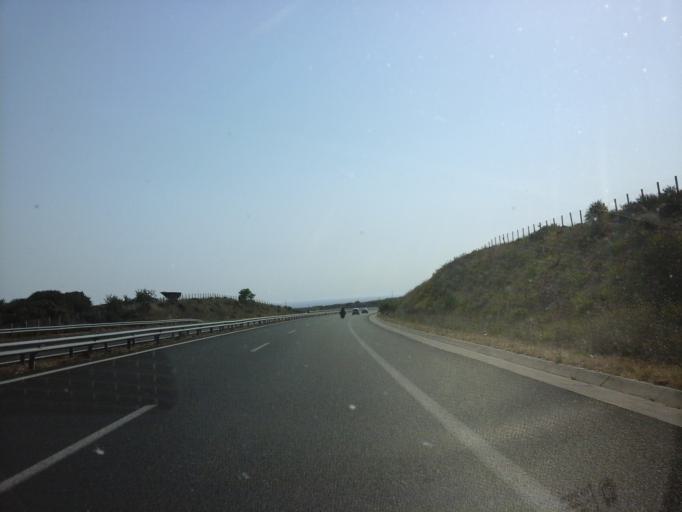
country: GR
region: East Macedonia and Thrace
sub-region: Nomos Evrou
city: Alexandroupoli
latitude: 40.8685
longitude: 25.8345
